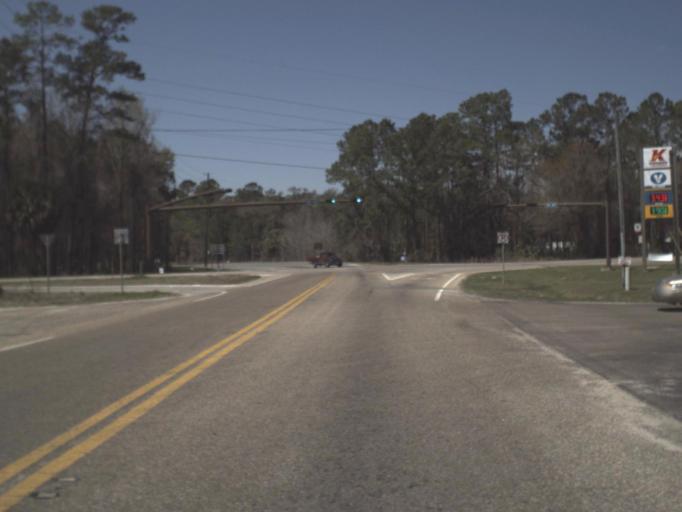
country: US
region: Florida
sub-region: Leon County
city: Woodville
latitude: 30.2321
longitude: -84.2291
